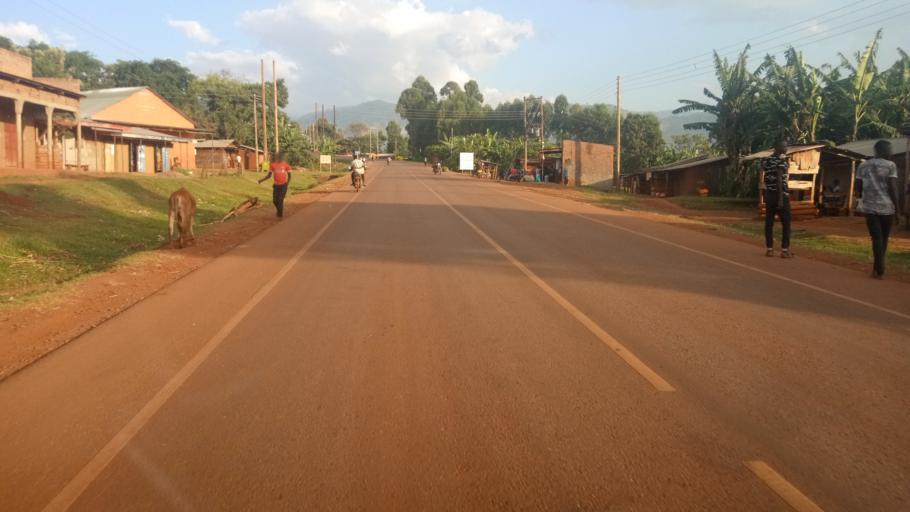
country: UG
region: Eastern Region
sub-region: Sironko District
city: Sironko
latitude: 1.3204
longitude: 34.3376
